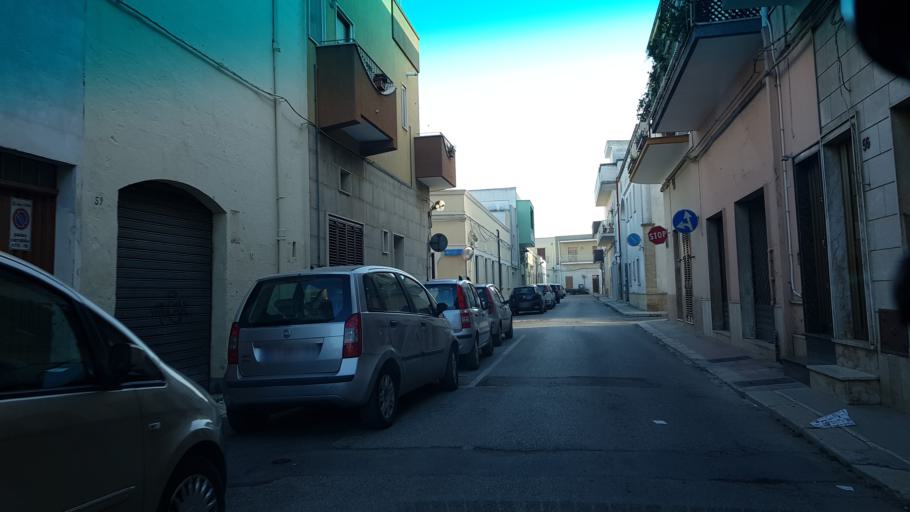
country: IT
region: Apulia
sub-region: Provincia di Brindisi
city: Mesagne
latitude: 40.5592
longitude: 17.8040
